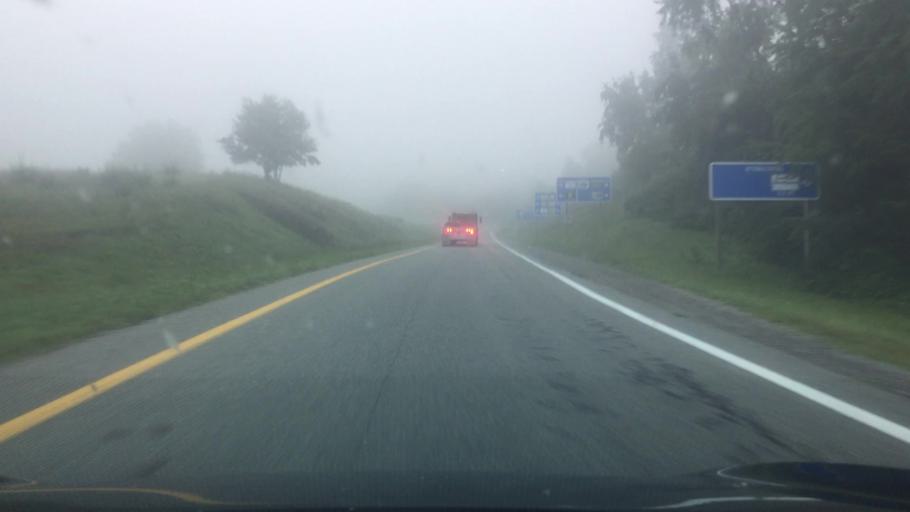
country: US
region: Virginia
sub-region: Pulaski County
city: Dublin
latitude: 37.0763
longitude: -80.6959
